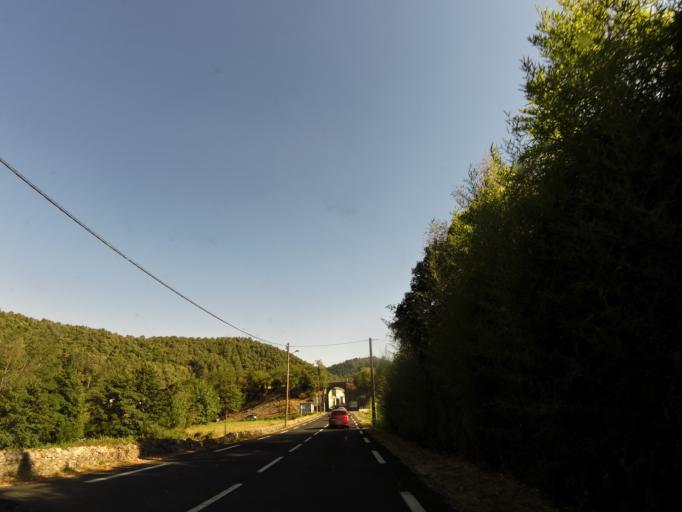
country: FR
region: Languedoc-Roussillon
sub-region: Departement du Gard
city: Sumene
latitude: 43.9996
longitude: 3.6760
